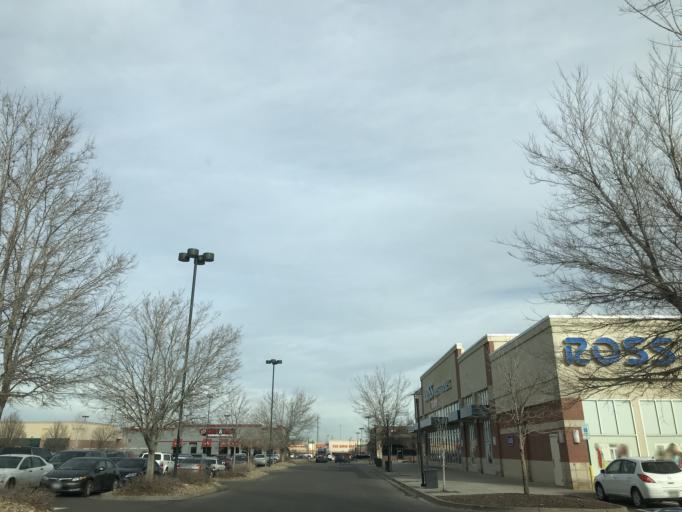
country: US
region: Colorado
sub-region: Adams County
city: Commerce City
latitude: 39.7665
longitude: -104.9008
